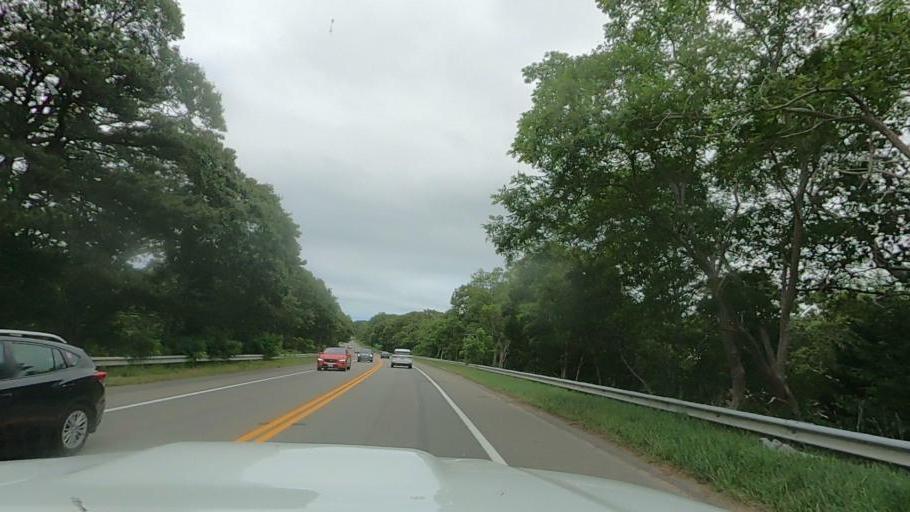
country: US
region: Massachusetts
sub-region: Barnstable County
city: Wellfleet
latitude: 41.9183
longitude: -70.0029
